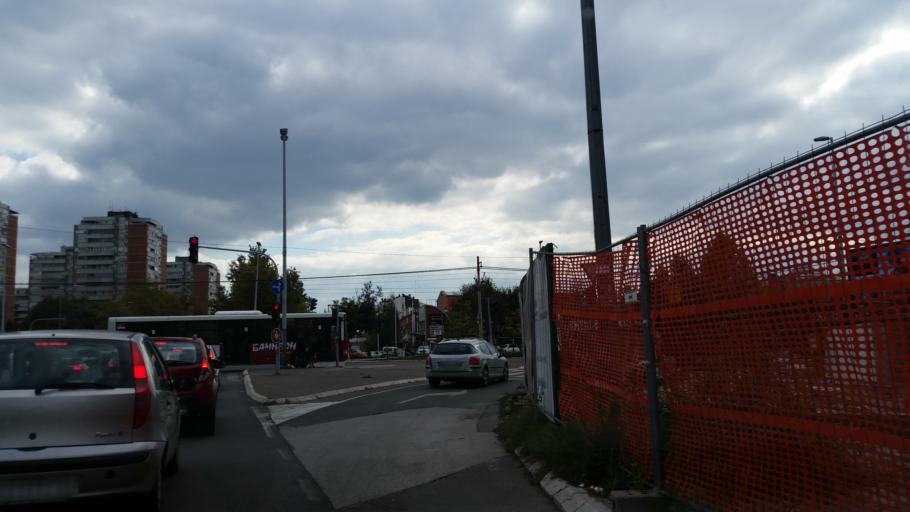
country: RS
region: Central Serbia
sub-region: Belgrade
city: Novi Beograd
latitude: 44.8038
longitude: 20.3877
